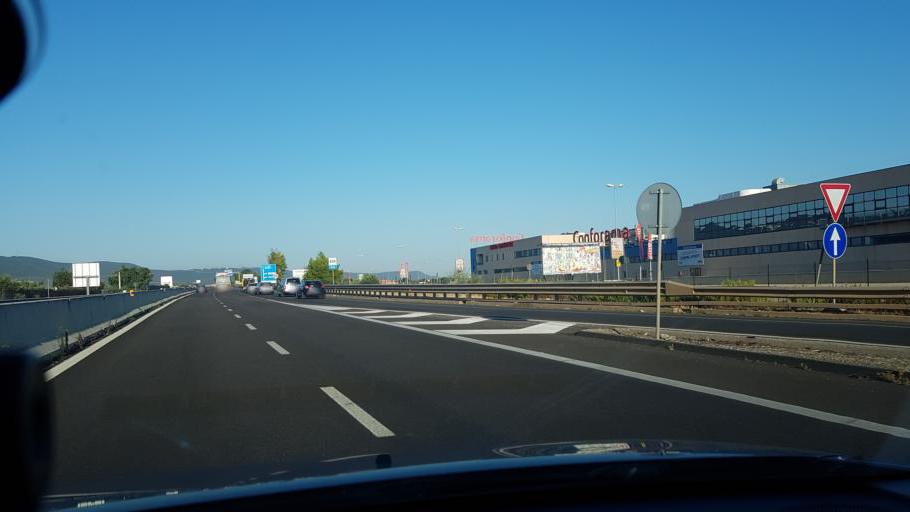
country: IT
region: Apulia
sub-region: Provincia di Brindisi
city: Fasano
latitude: 40.8379
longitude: 17.3804
